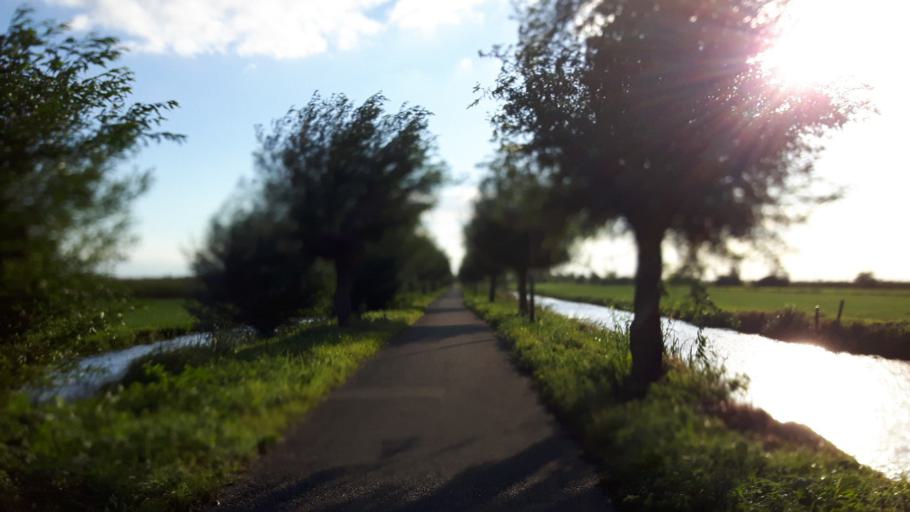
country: NL
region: Utrecht
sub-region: Gemeente Woerden
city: Woerden
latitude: 52.0684
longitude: 4.8747
